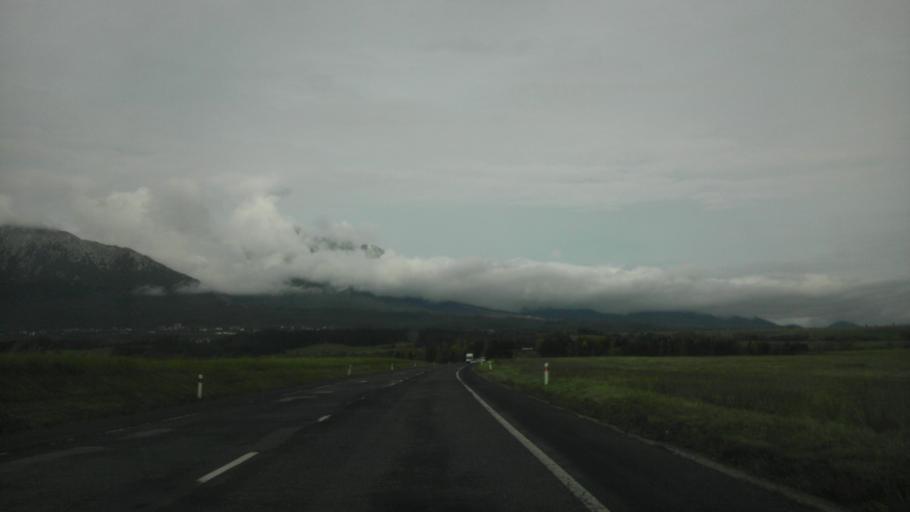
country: SK
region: Presovsky
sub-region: Okres Poprad
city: Nova Lesna
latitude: 49.0937
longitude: 20.2605
